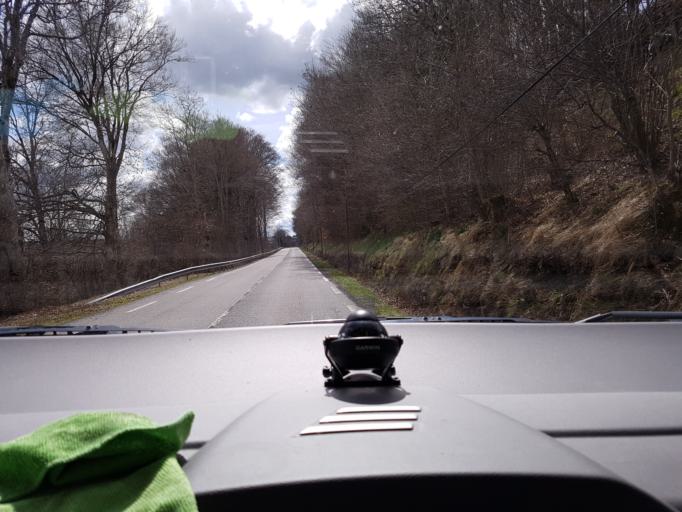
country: FR
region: Midi-Pyrenees
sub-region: Departement de l'Aveyron
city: Laguiole
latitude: 44.6974
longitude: 2.8638
